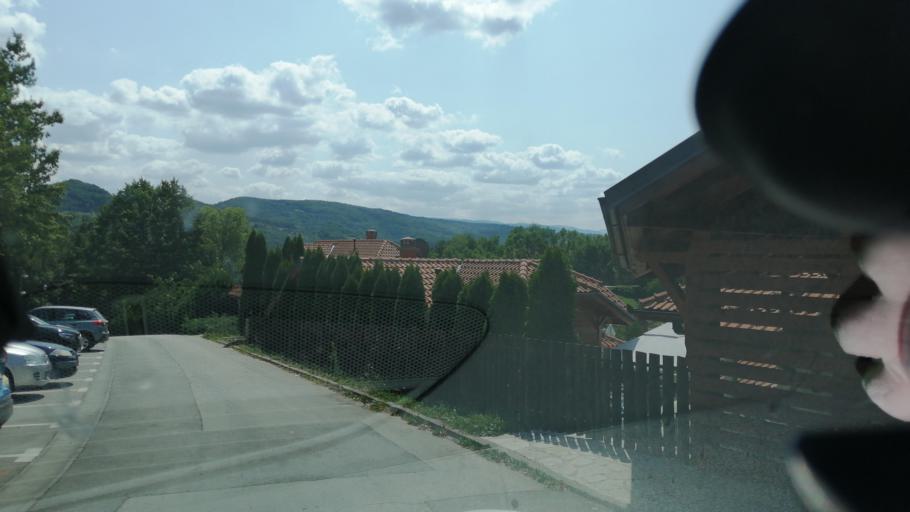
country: RS
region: Central Serbia
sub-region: Moravicki Okrug
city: Ivanjica
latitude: 43.6176
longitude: 20.2478
